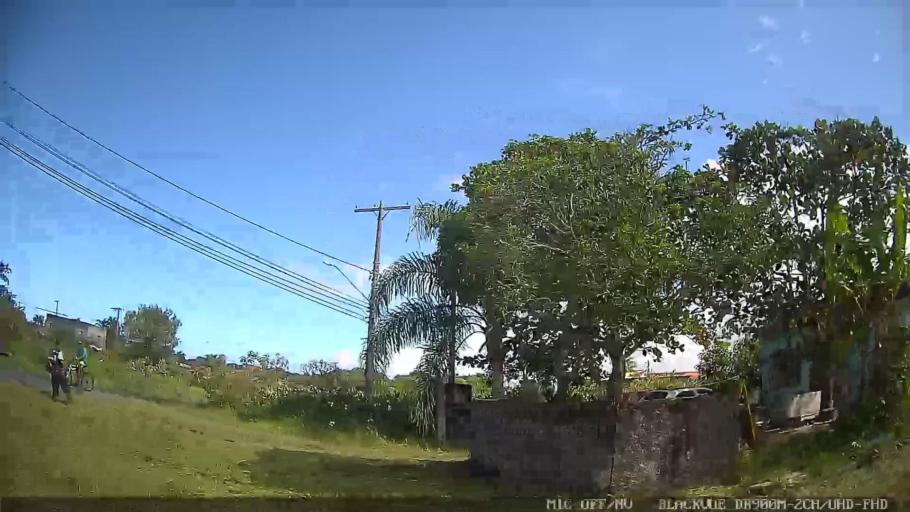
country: BR
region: Sao Paulo
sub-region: Itanhaem
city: Itanhaem
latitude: -24.2278
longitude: -46.8784
